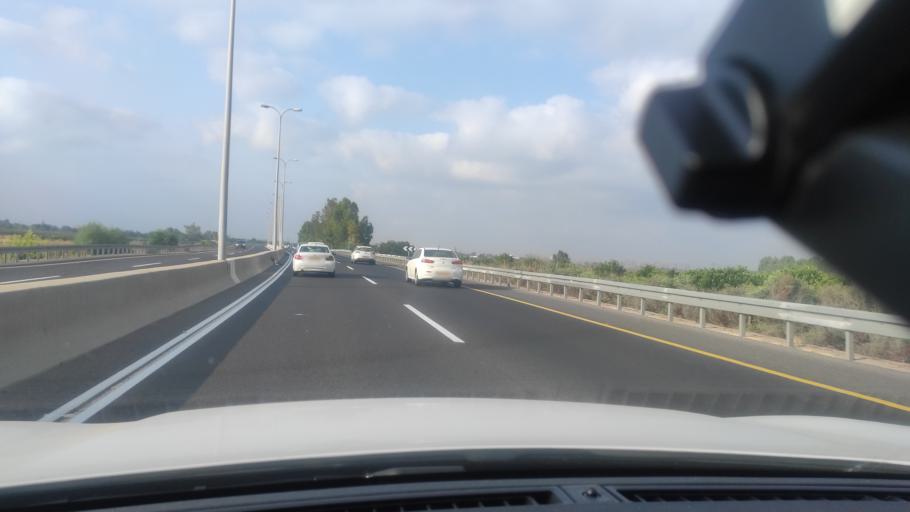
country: IL
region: Central District
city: Hod HaSharon
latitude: 32.1446
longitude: 34.9180
